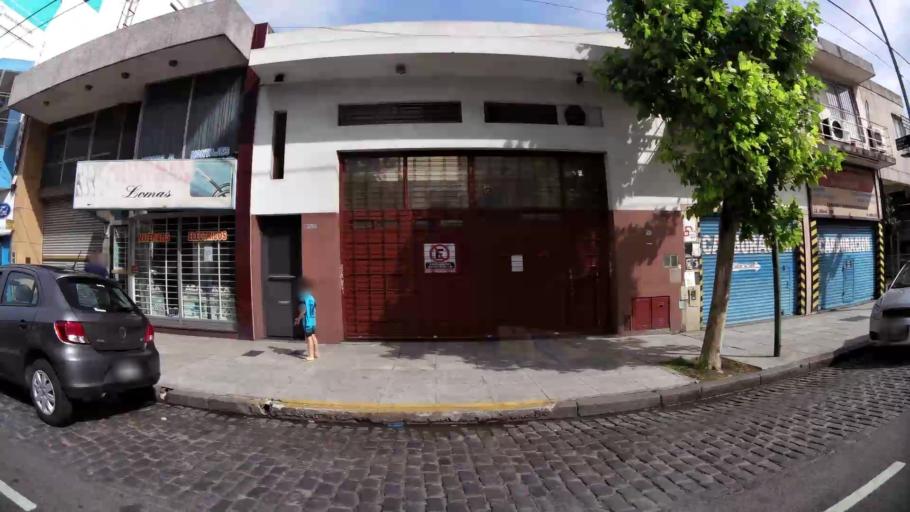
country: AR
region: Buenos Aires F.D.
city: Villa Lugano
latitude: -34.6608
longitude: -58.5152
